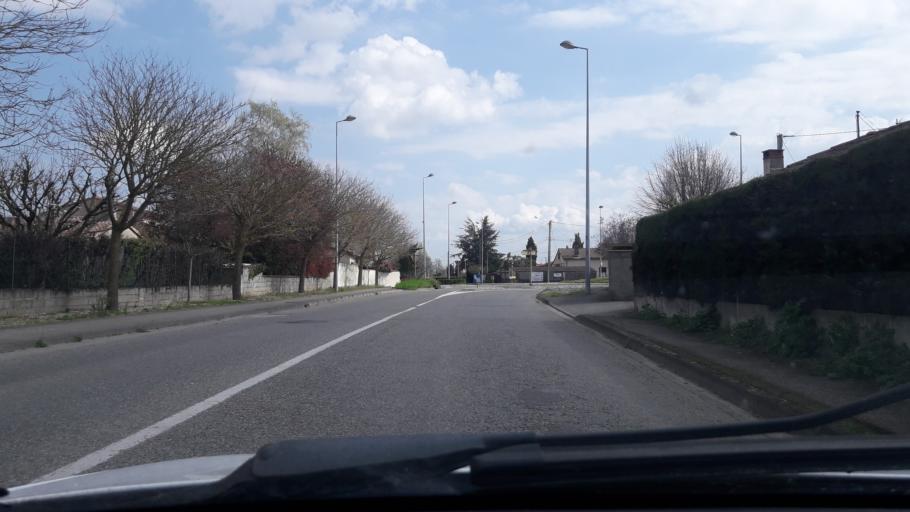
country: FR
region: Midi-Pyrenees
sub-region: Departement de la Haute-Garonne
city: Seysses
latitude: 43.4963
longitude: 1.3029
